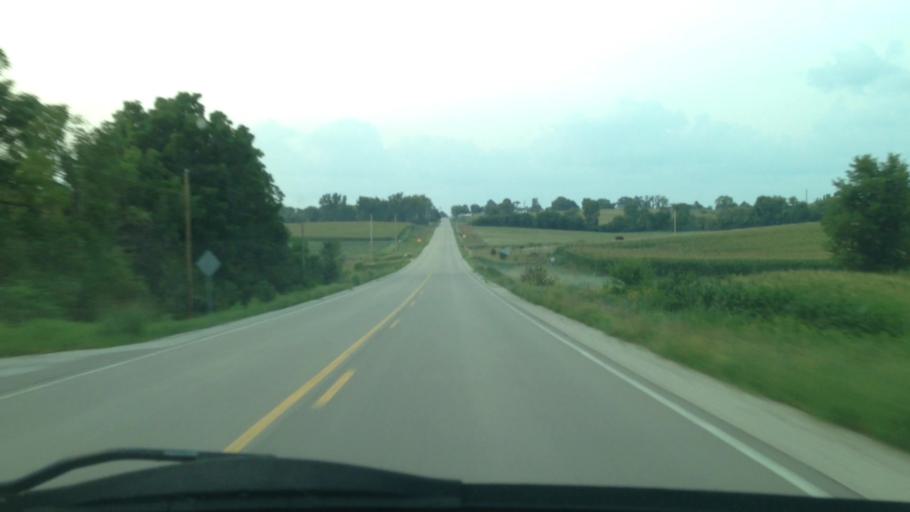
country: US
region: Iowa
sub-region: Benton County
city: Urbana
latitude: 42.2132
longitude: -91.8714
